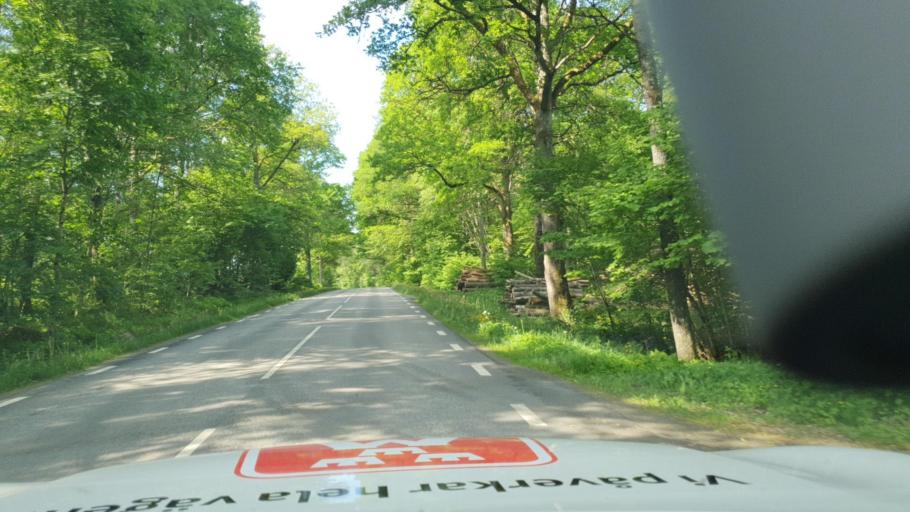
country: SE
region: Vaestra Goetaland
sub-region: Herrljunga Kommun
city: Herrljunga
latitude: 58.0011
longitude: 13.1066
